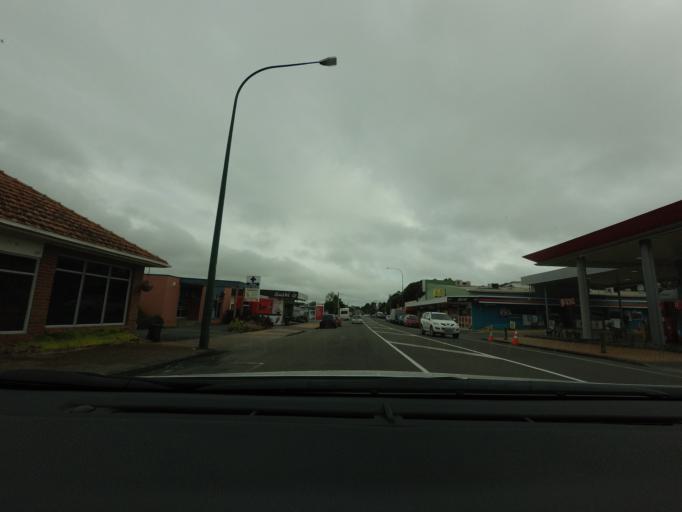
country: NZ
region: Auckland
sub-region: Auckland
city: Wellsford
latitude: -36.2965
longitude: 174.5235
